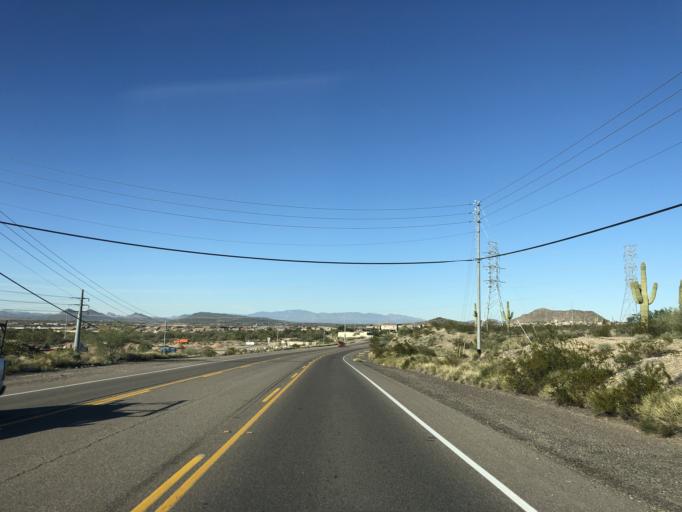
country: US
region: Arizona
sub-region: Maricopa County
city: Sun City West
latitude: 33.7041
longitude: -112.2898
